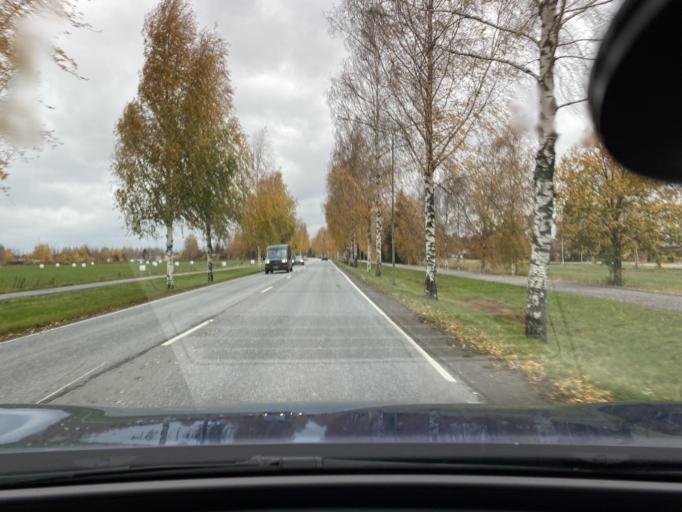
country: FI
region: Satakunta
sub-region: Pori
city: Kokemaeki
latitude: 61.2577
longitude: 22.3348
